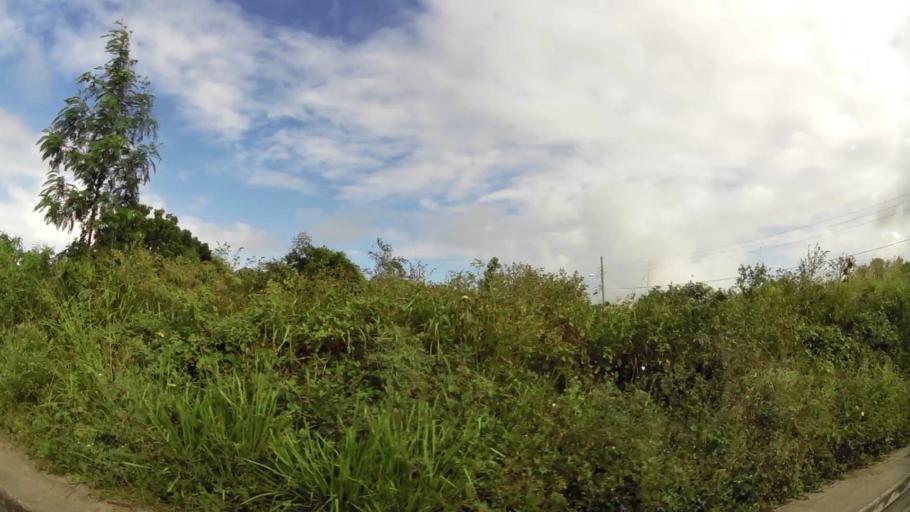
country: AG
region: Saint George
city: Piggotts
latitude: 17.1305
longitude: -61.8224
